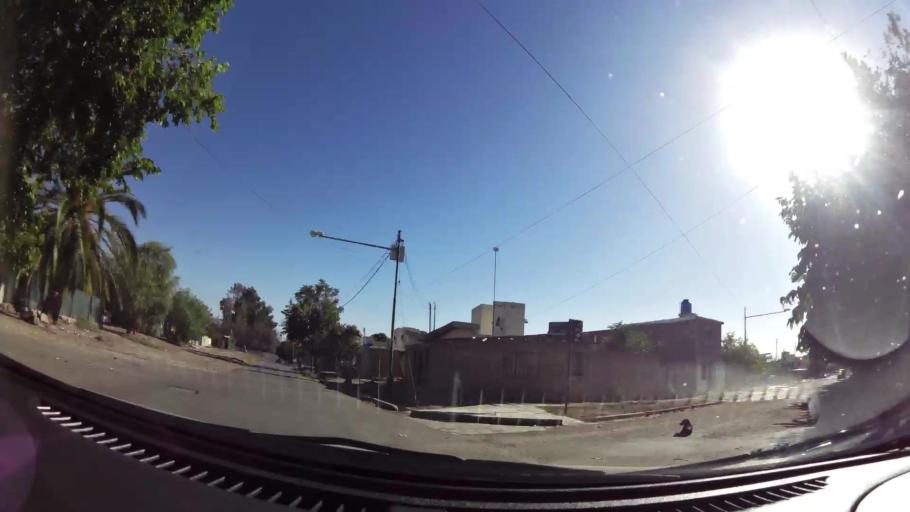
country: AR
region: Mendoza
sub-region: Departamento de Godoy Cruz
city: Godoy Cruz
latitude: -32.9268
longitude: -68.8669
